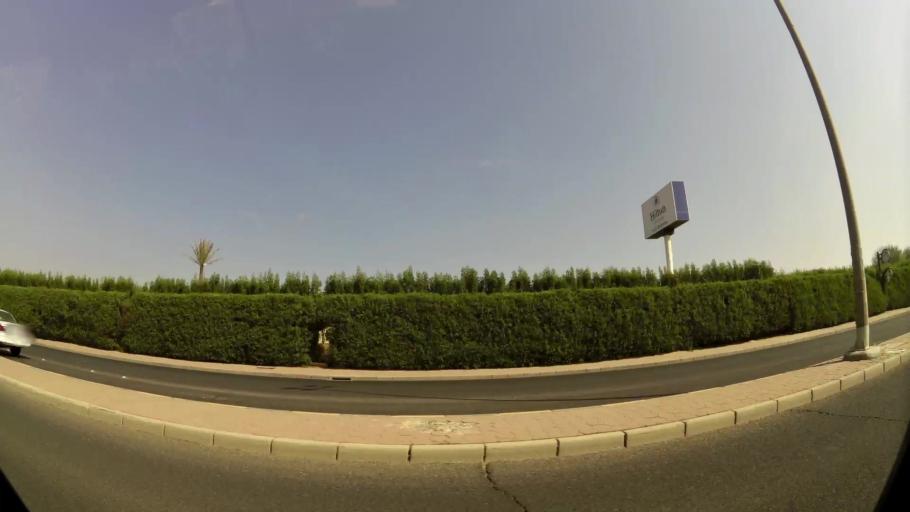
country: KW
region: Al Ahmadi
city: Al Manqaf
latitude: 29.1142
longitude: 48.1353
